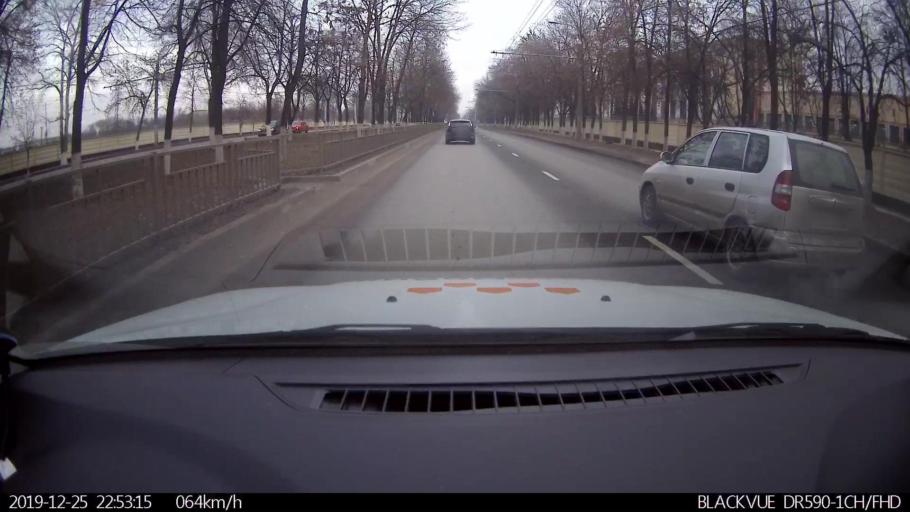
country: RU
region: Nizjnij Novgorod
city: Gorbatovka
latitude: 56.2502
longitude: 43.8848
